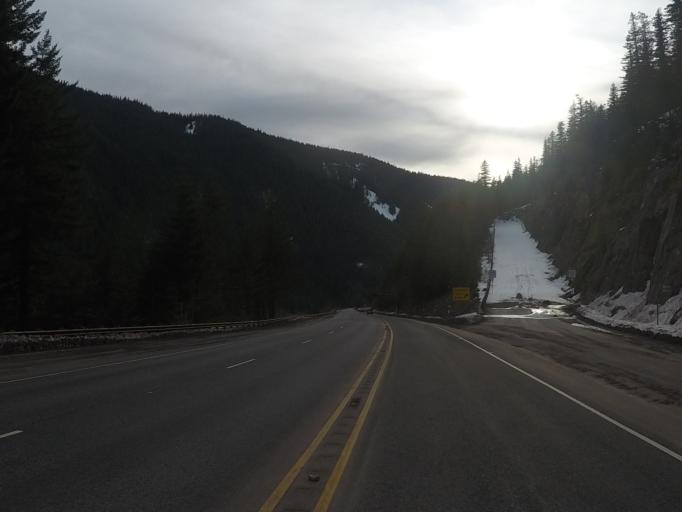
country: US
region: Oregon
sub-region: Clackamas County
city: Mount Hood Village
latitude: 45.3060
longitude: -121.8149
